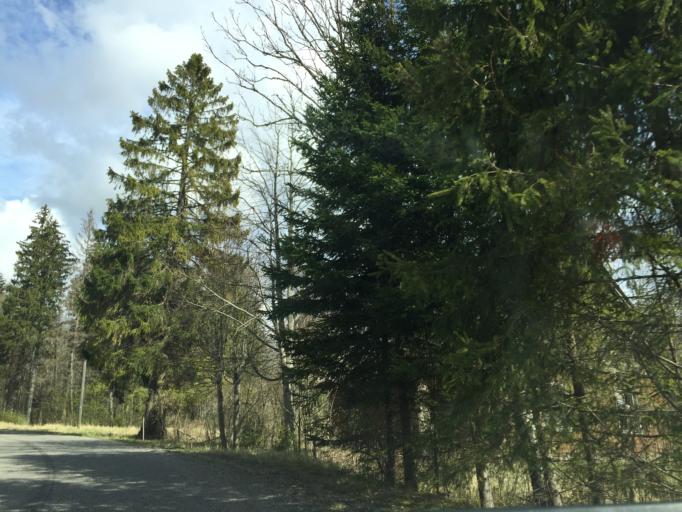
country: LV
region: Limbazu Rajons
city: Limbazi
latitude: 57.6135
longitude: 24.6850
